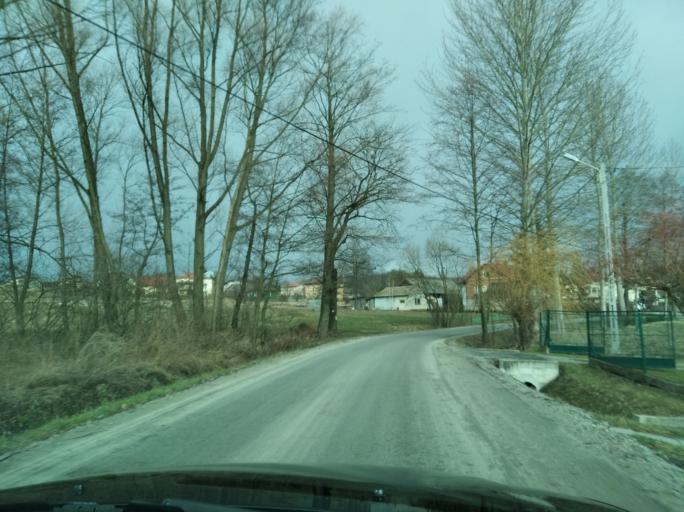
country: PL
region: Subcarpathian Voivodeship
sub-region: Powiat rzeszowski
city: Hyzne
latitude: 49.9072
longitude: 22.1970
